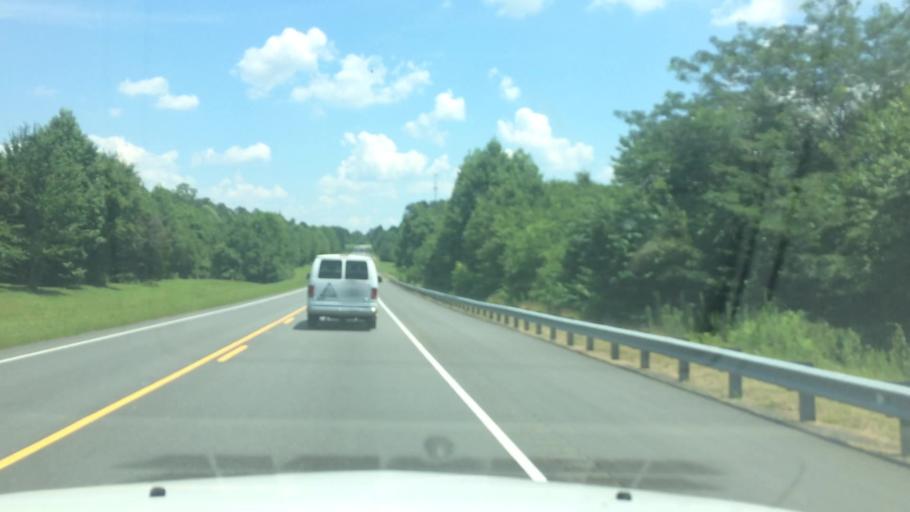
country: US
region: North Carolina
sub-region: Iredell County
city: Statesville
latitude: 35.8030
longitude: -80.9549
